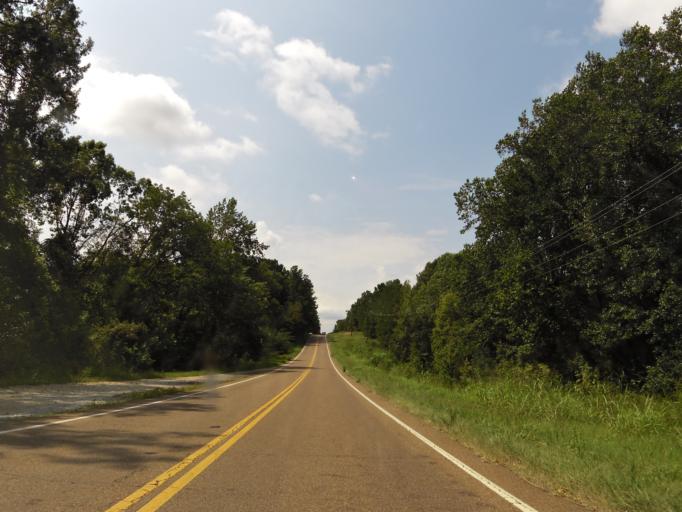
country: US
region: Tennessee
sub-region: Decatur County
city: Decaturville
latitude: 35.5728
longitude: -88.1411
